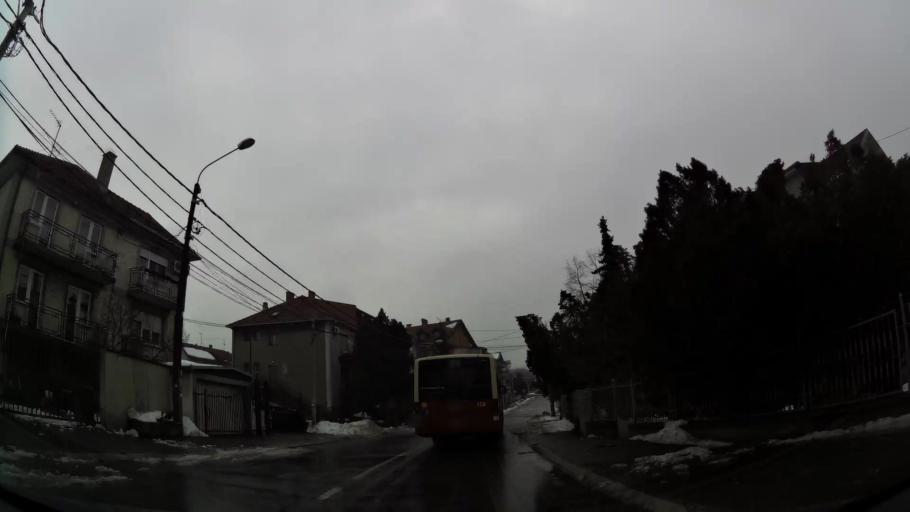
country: RS
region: Central Serbia
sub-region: Belgrade
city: Zvezdara
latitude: 44.7588
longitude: 20.5256
